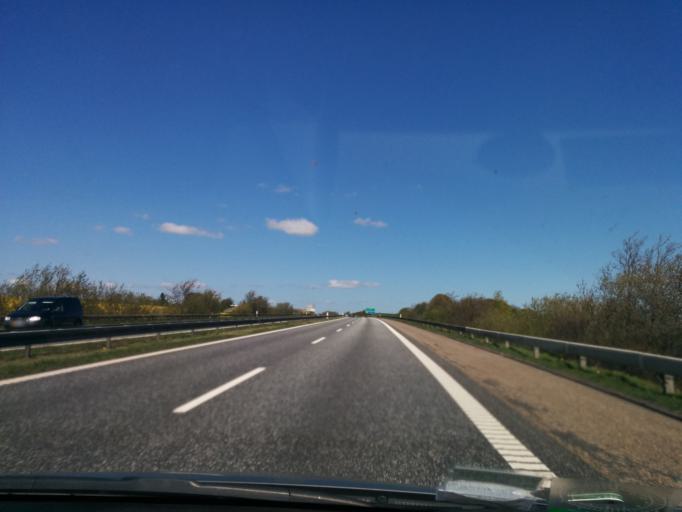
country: DK
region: Central Jutland
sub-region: Favrskov Kommune
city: Hadsten
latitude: 56.3241
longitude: 10.1222
